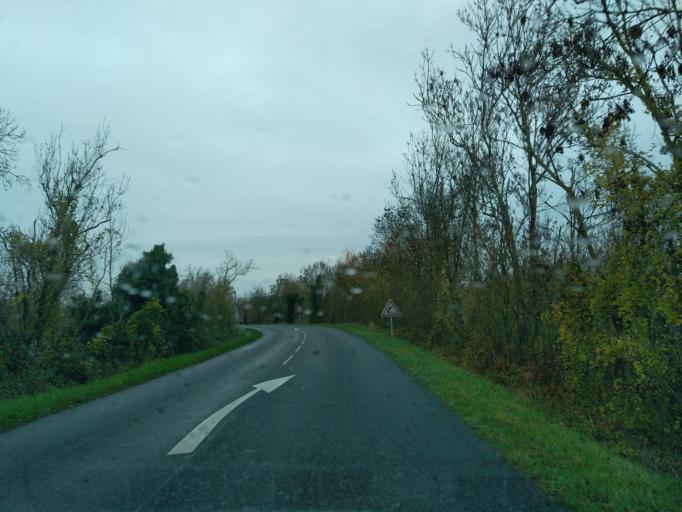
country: FR
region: Pays de la Loire
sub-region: Departement de la Vendee
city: Maillezais
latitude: 46.3230
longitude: -0.7872
